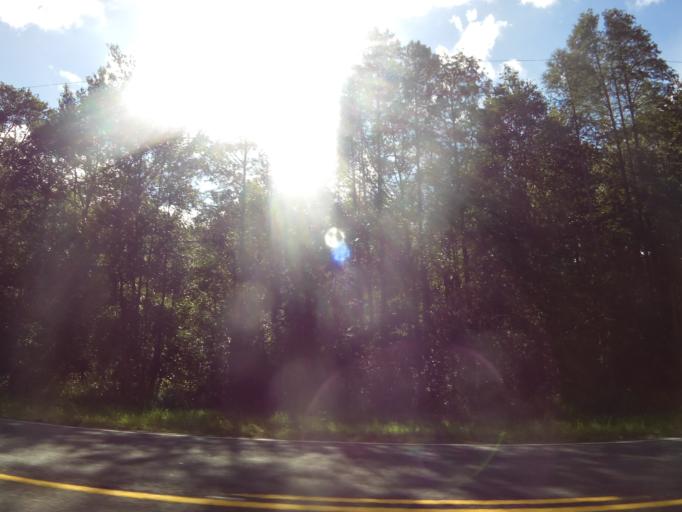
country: US
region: Georgia
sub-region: Camden County
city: Woodbine
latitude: 31.0155
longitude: -81.7314
